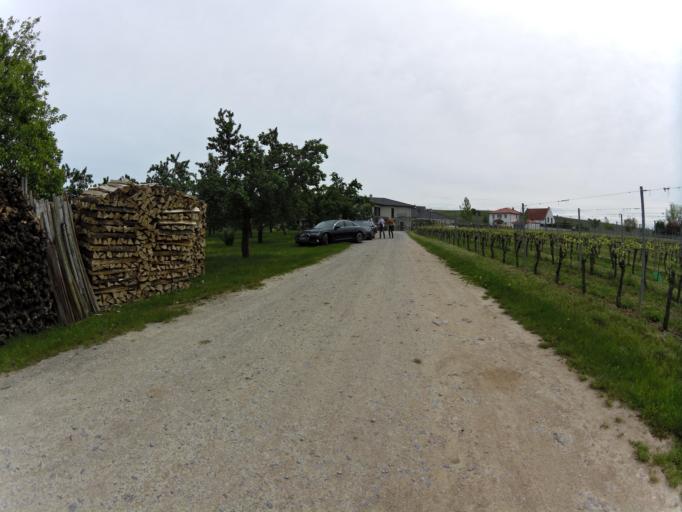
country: DE
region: Bavaria
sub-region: Regierungsbezirk Unterfranken
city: Nordheim
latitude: 49.8570
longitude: 10.1804
